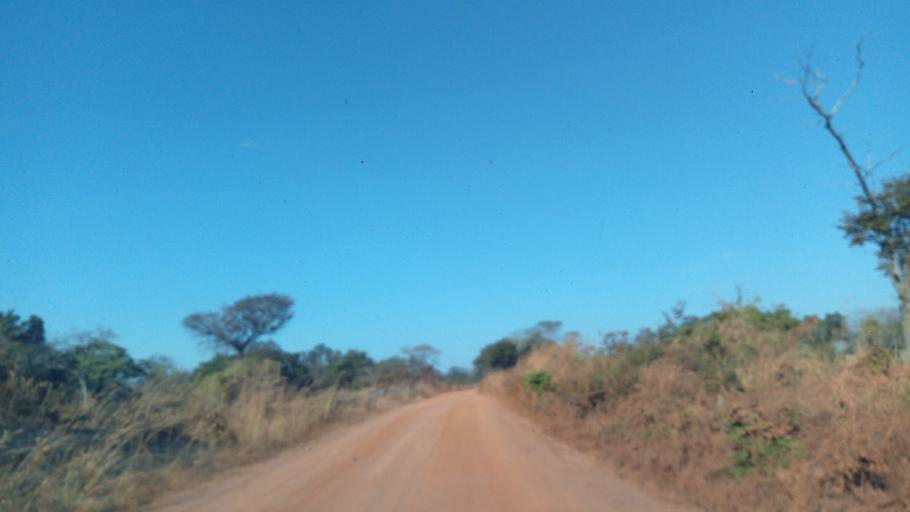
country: ZM
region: Luapula
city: Mwense
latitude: -10.5458
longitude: 28.4476
